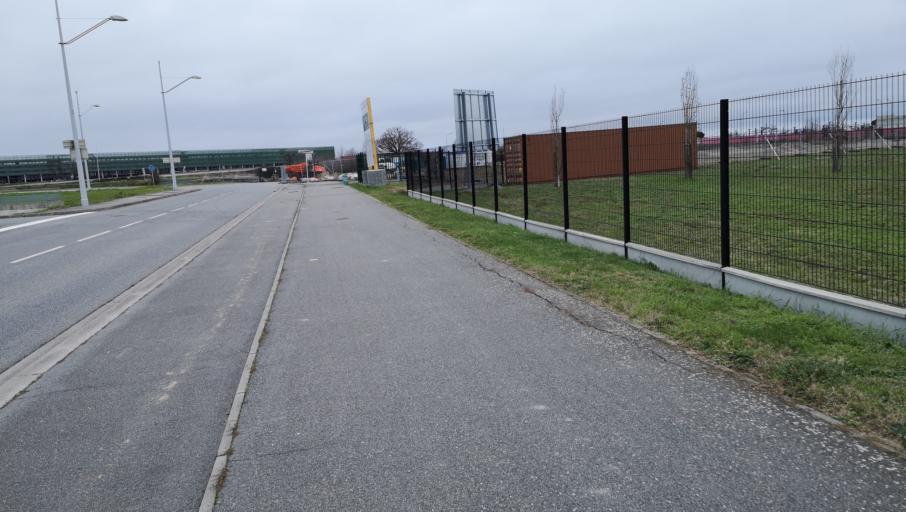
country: FR
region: Midi-Pyrenees
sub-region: Departement de la Haute-Garonne
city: Beauzelle
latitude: 43.6604
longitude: 1.3583
